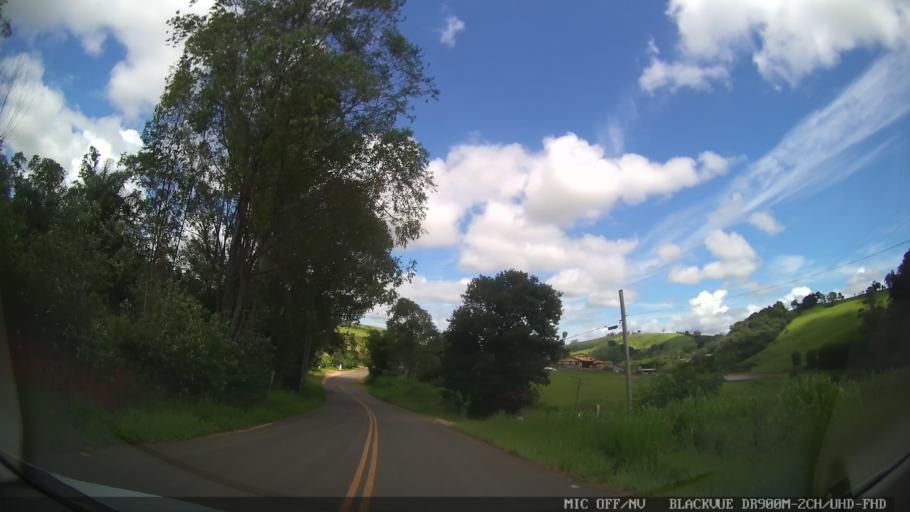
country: BR
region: Sao Paulo
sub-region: Braganca Paulista
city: Braganca Paulista
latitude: -22.8628
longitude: -46.6769
